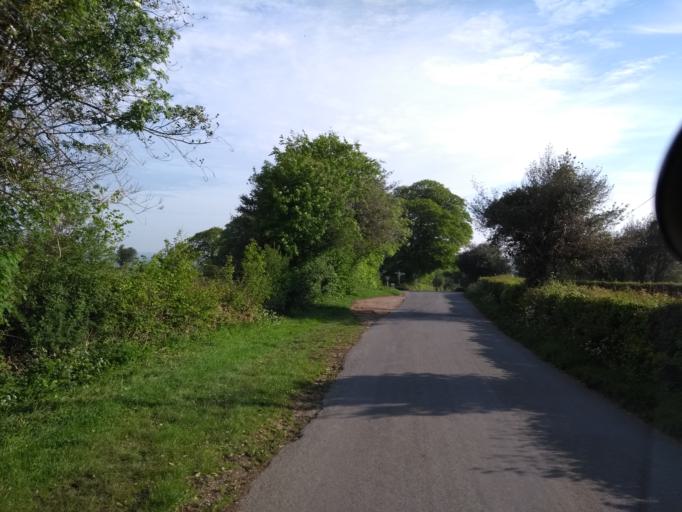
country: GB
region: England
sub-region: Dorset
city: Lyme Regis
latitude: 50.7940
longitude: -2.9272
